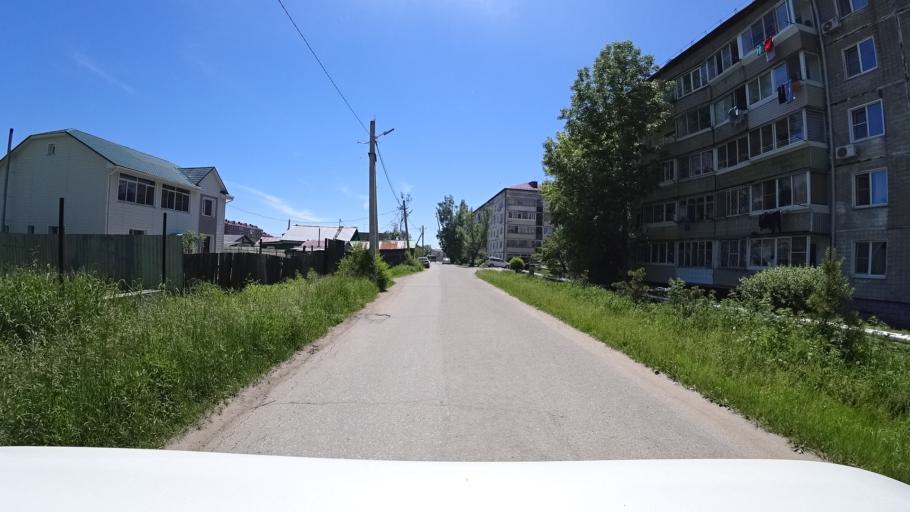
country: RU
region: Khabarovsk Krai
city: Topolevo
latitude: 48.5082
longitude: 135.1749
